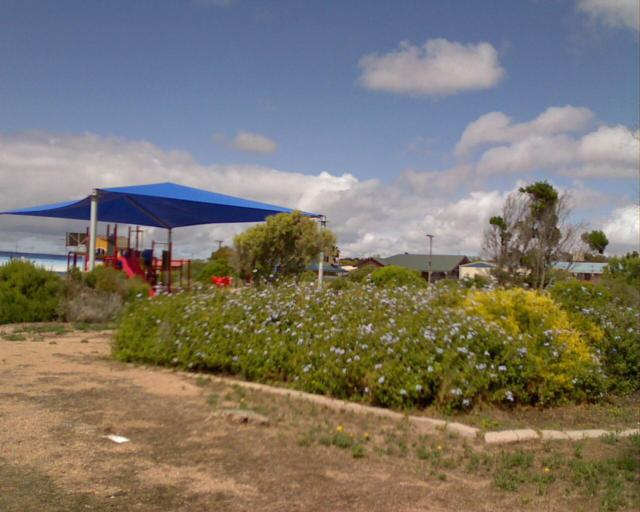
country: AU
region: South Australia
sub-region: Ceduna
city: Ceduna
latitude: -32.1012
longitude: 133.5790
